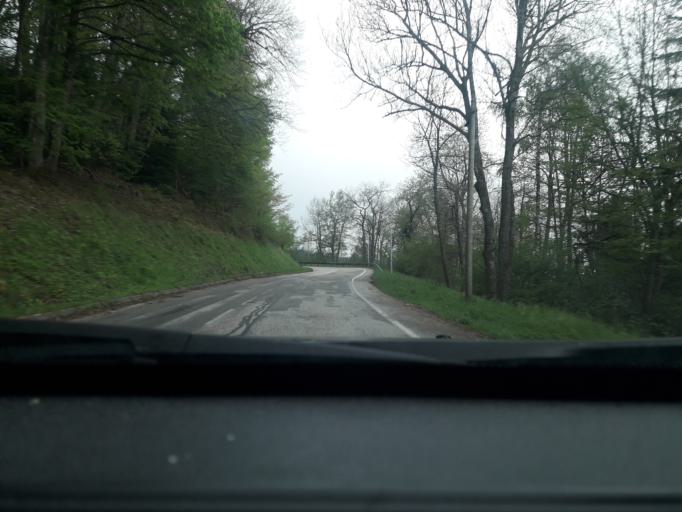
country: FR
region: Rhone-Alpes
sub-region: Departement de l'Isere
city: Vaulnaveys-le-Bas
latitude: 45.1150
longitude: 5.8355
